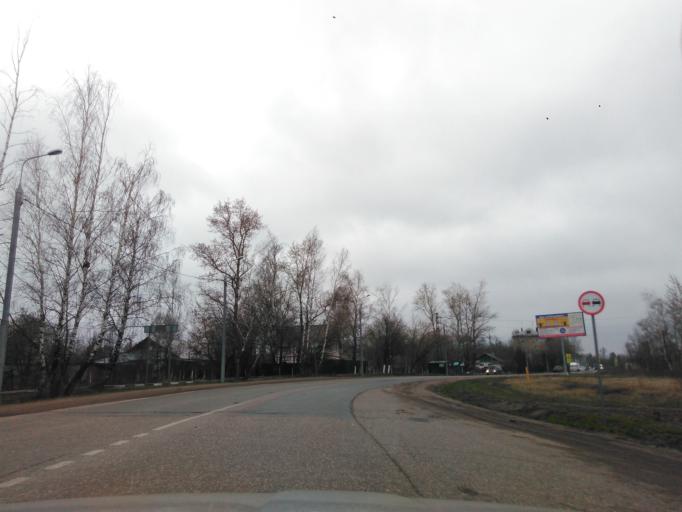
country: RU
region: Moskovskaya
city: Nakhabino
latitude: 55.8343
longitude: 37.1546
